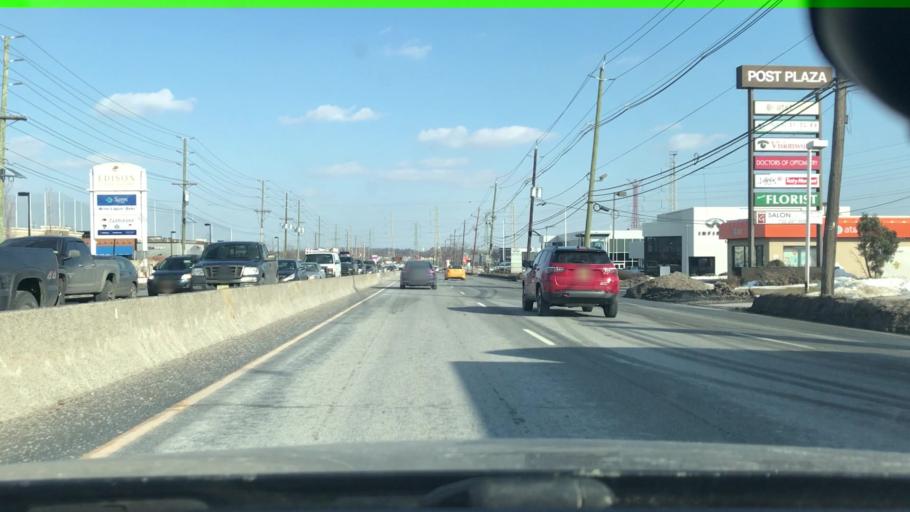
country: US
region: New Jersey
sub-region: Middlesex County
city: Piscataway
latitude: 40.5154
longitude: -74.3743
